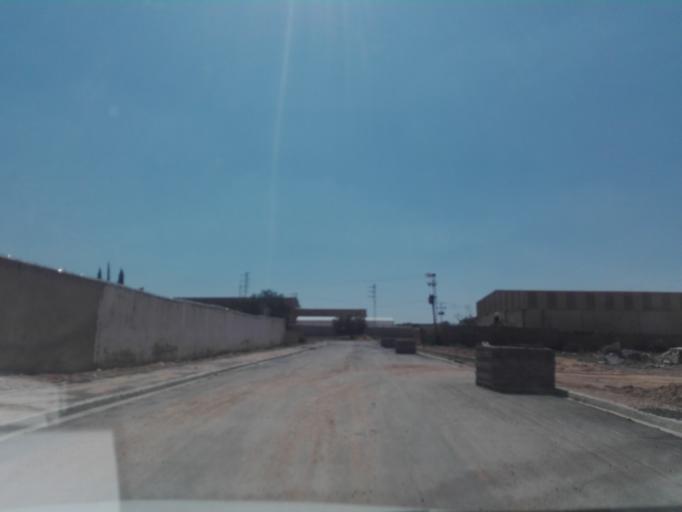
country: TN
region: Safaqis
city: Sfax
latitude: 34.7242
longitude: 10.5142
